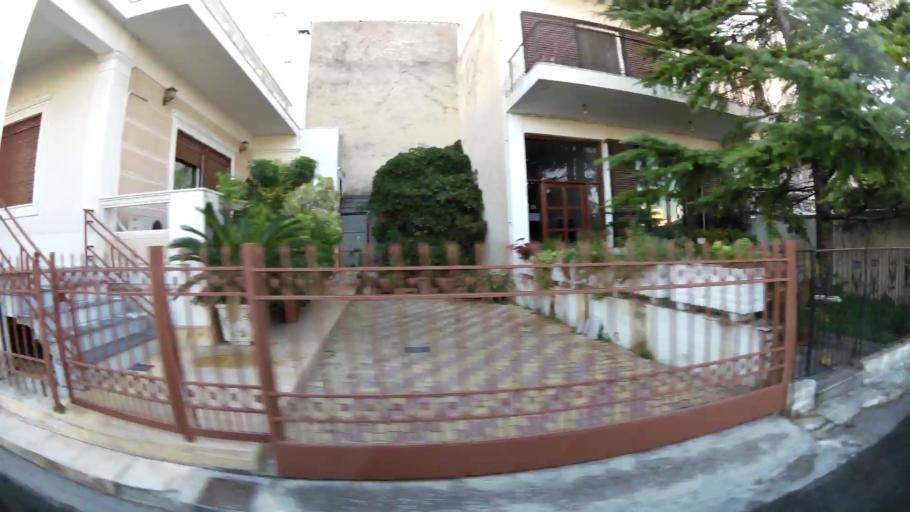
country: GR
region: Attica
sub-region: Nomarchia Anatolikis Attikis
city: Spata
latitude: 37.9604
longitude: 23.9121
